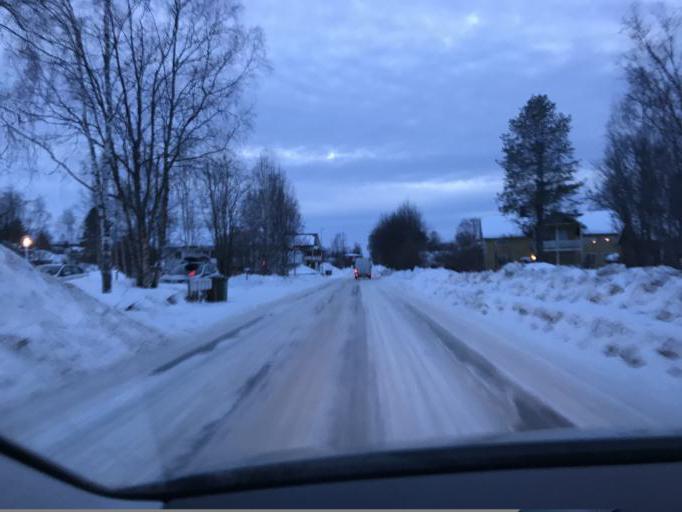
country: SE
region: Norrbotten
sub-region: Lulea Kommun
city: Sodra Sunderbyn
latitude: 65.6611
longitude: 21.9450
